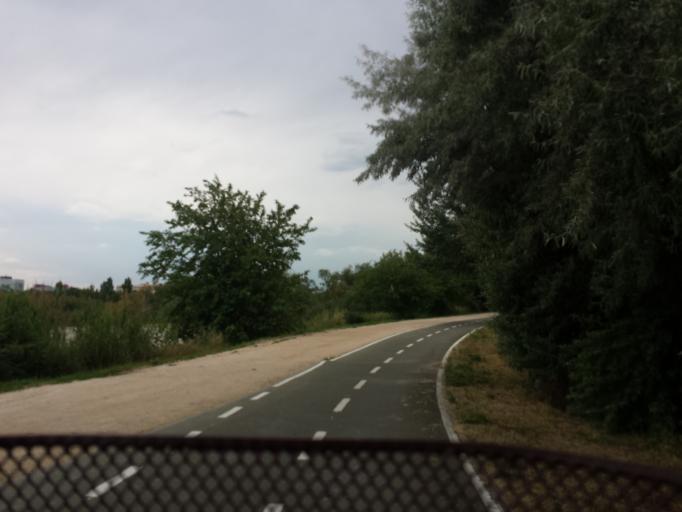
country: ES
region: Aragon
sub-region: Provincia de Zaragoza
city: Almozara
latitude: 41.6792
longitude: -0.9022
